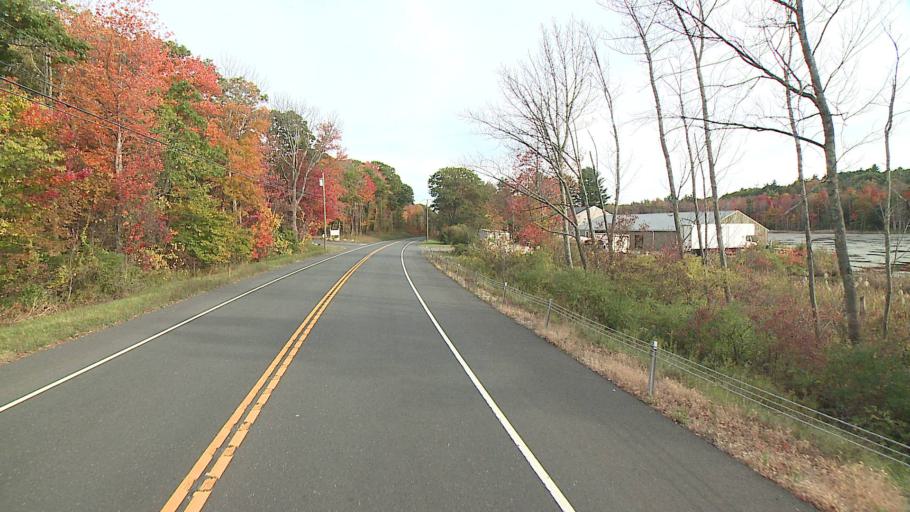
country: US
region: Connecticut
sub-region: Litchfield County
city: Winchester Center
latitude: 41.9788
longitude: -73.1513
